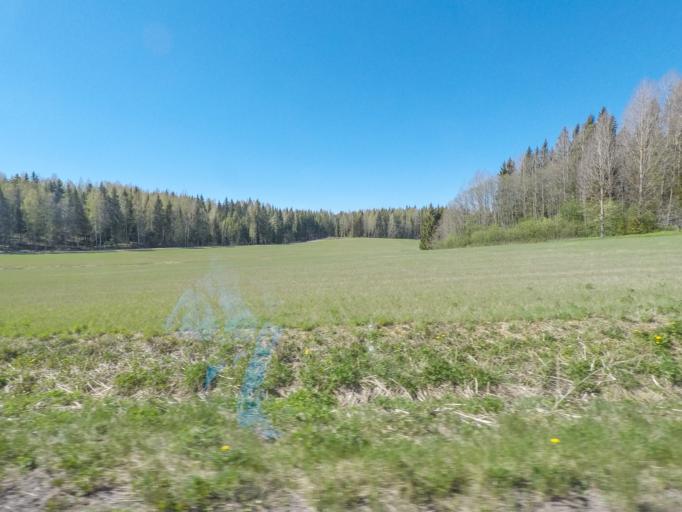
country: FI
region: Uusimaa
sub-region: Helsinki
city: Sammatti
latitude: 60.4014
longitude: 23.8177
